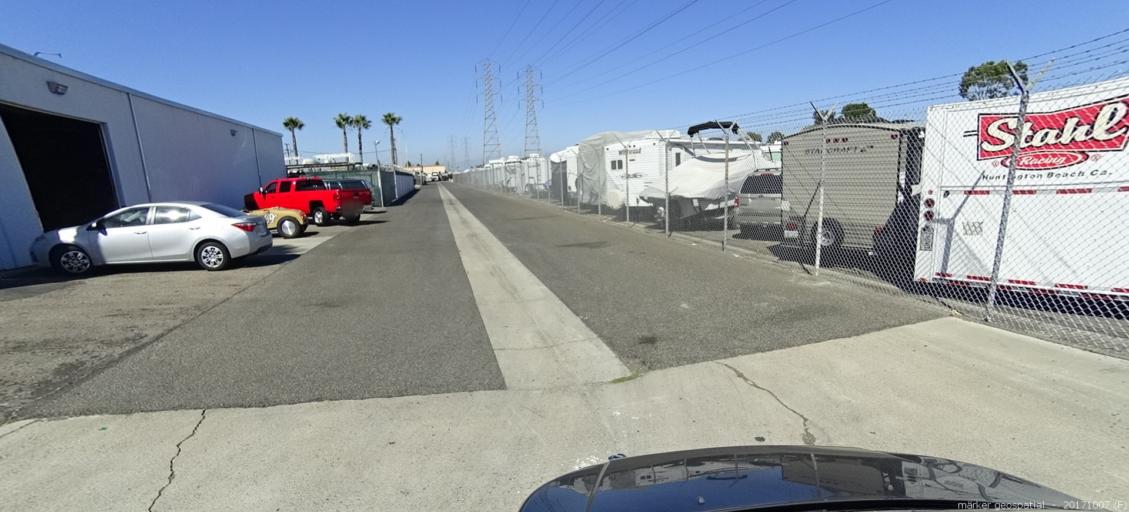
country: US
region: California
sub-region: Orange County
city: Westminster
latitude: 33.7749
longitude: -117.9997
